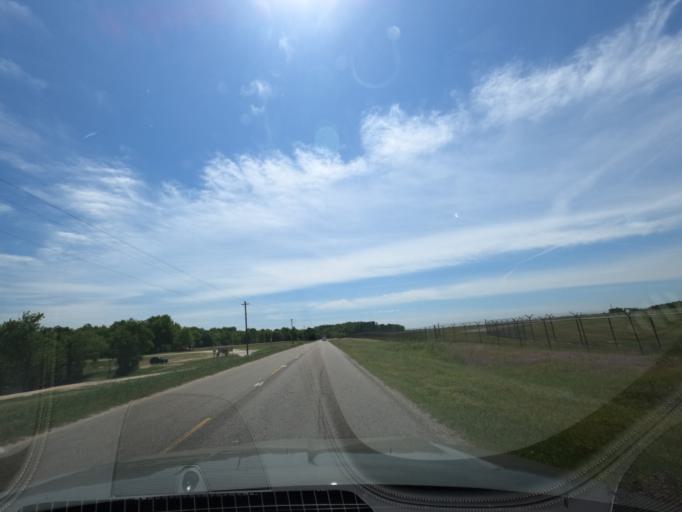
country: US
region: Georgia
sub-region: Richmond County
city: Augusta
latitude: 33.3887
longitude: -81.9717
